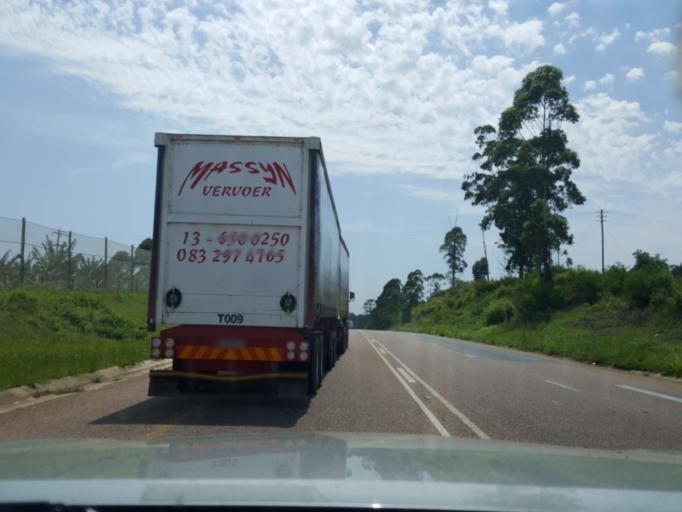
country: ZA
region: Mpumalanga
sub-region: Ehlanzeni District
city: White River
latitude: -25.1148
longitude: 31.0544
